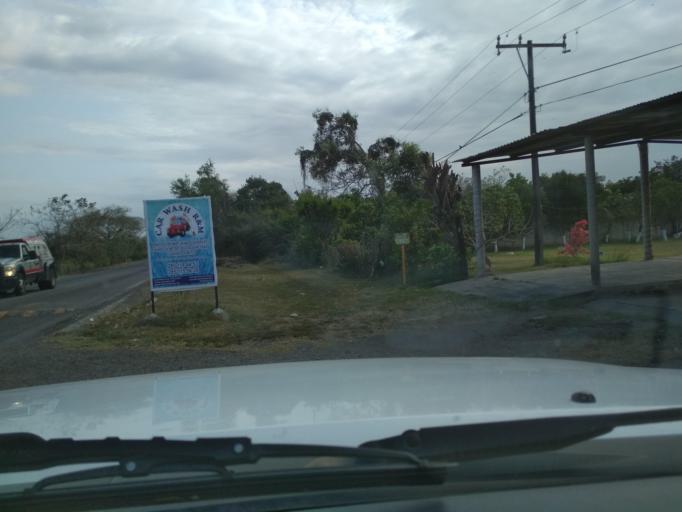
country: MX
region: Veracruz
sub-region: Veracruz
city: Delfino Victoria (Santa Fe)
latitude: 19.1490
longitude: -96.2992
